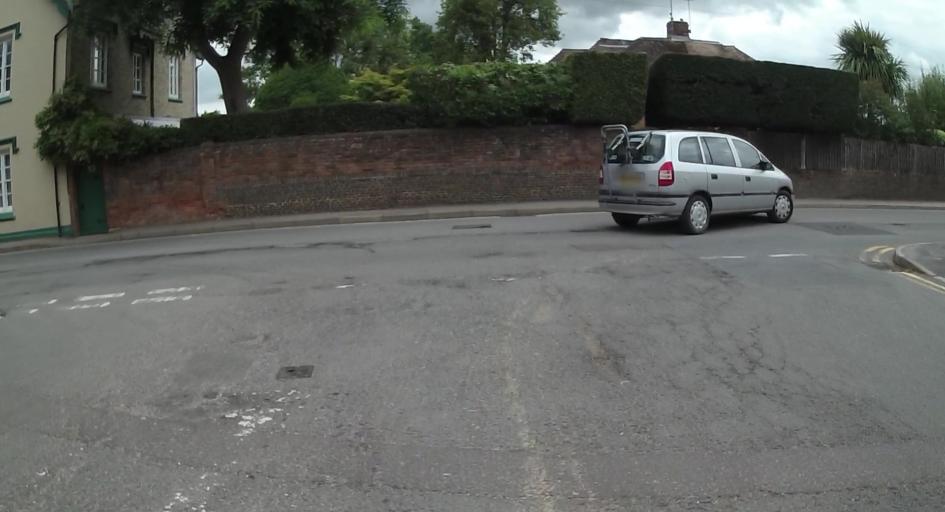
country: GB
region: England
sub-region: Surrey
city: Farnham
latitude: 51.2120
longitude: -0.8076
